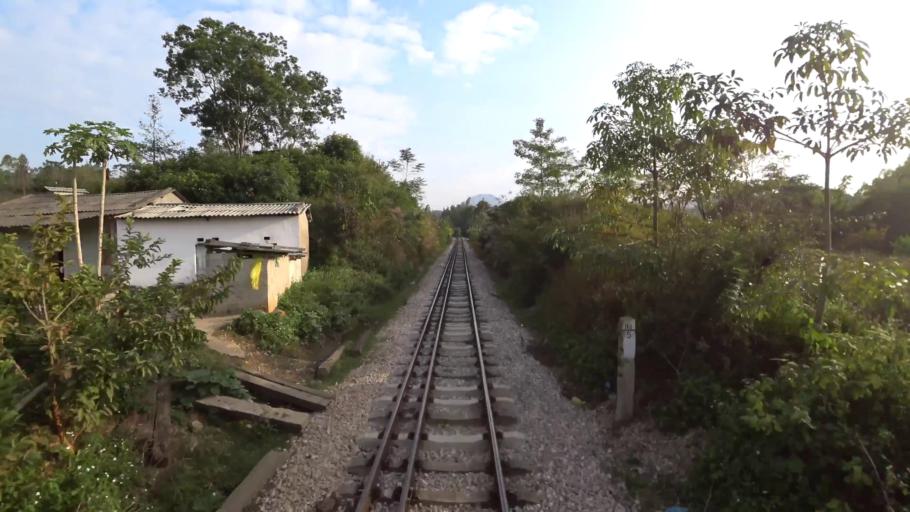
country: VN
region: Lang Son
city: Thi Tran Cao Loc
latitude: 21.9295
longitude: 106.7018
